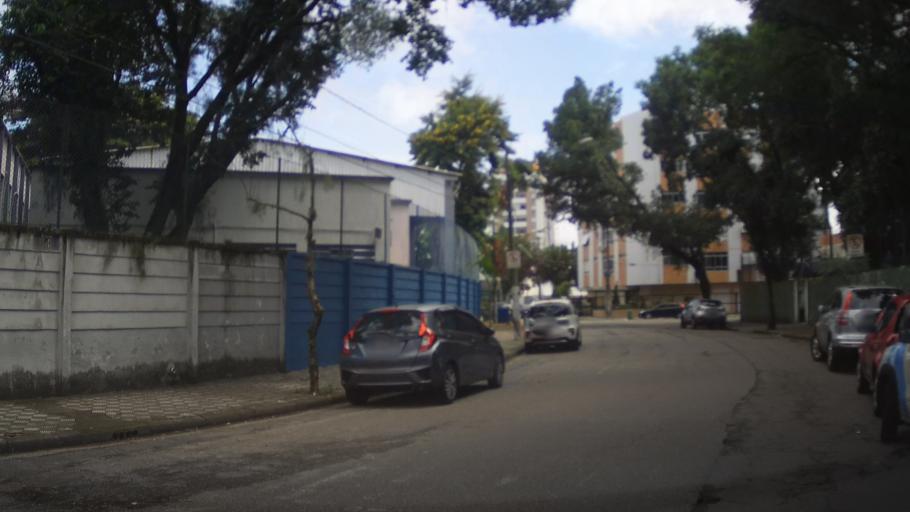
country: BR
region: Sao Paulo
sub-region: Santos
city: Santos
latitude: -23.9796
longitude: -46.2992
